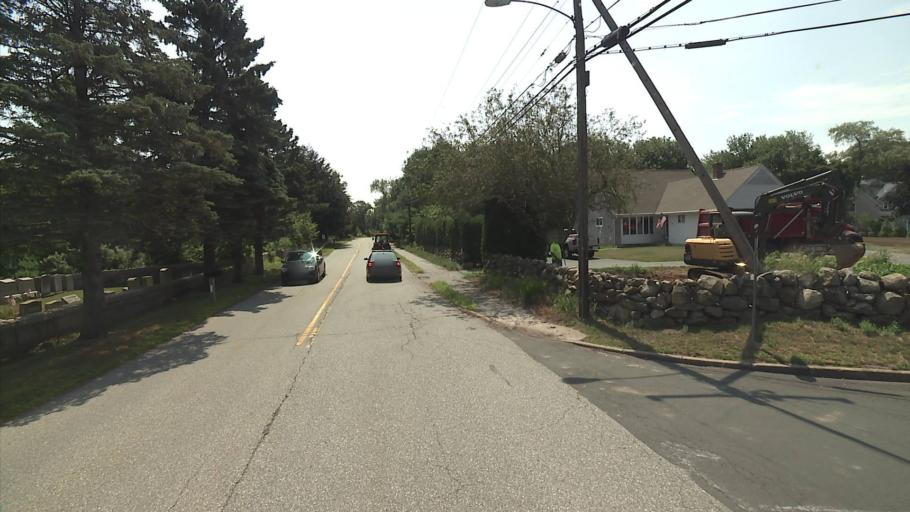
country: US
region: Connecticut
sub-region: New London County
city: Central Waterford
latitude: 41.3096
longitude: -72.1292
